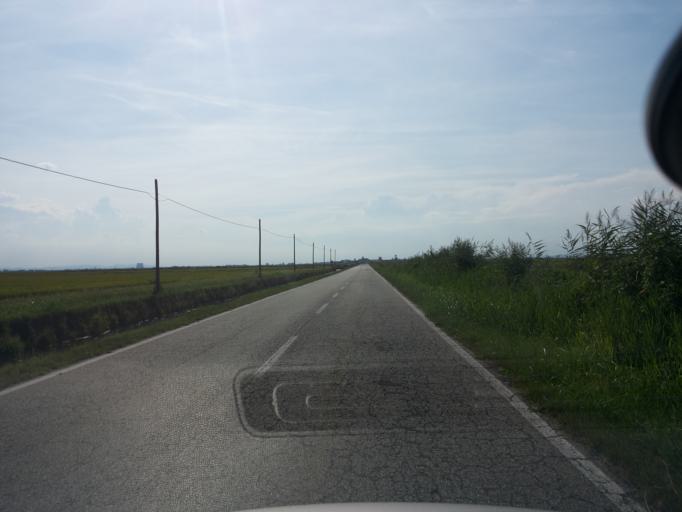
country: IT
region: Piedmont
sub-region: Provincia di Vercelli
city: Sali Vercellese
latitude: 45.2920
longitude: 8.3204
